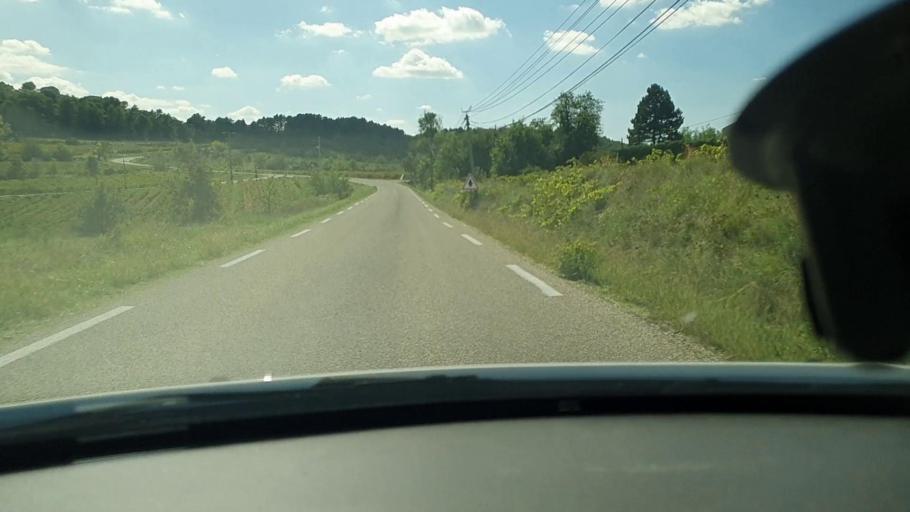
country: FR
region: Languedoc-Roussillon
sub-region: Departement du Gard
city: Goudargues
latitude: 44.1575
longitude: 4.4862
